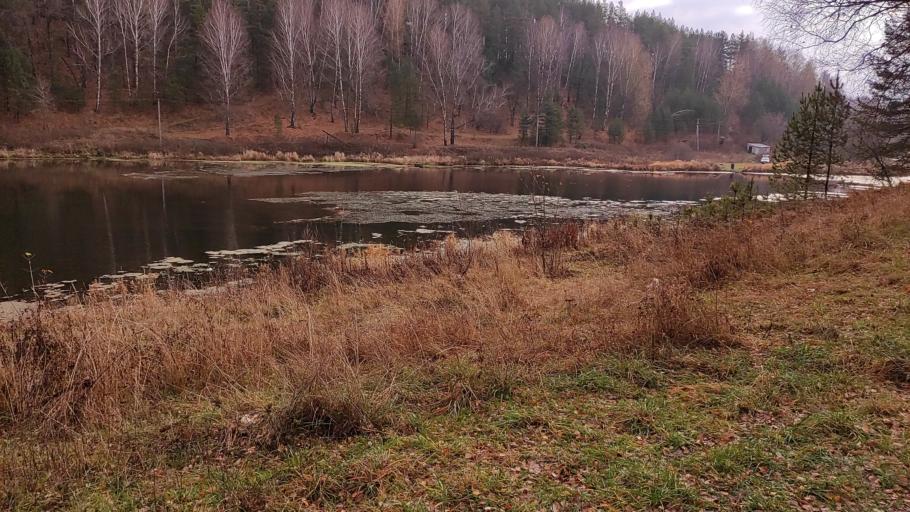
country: RU
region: Ulyanovsk
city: Krasnyy Gulyay
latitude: 54.0780
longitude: 48.3043
